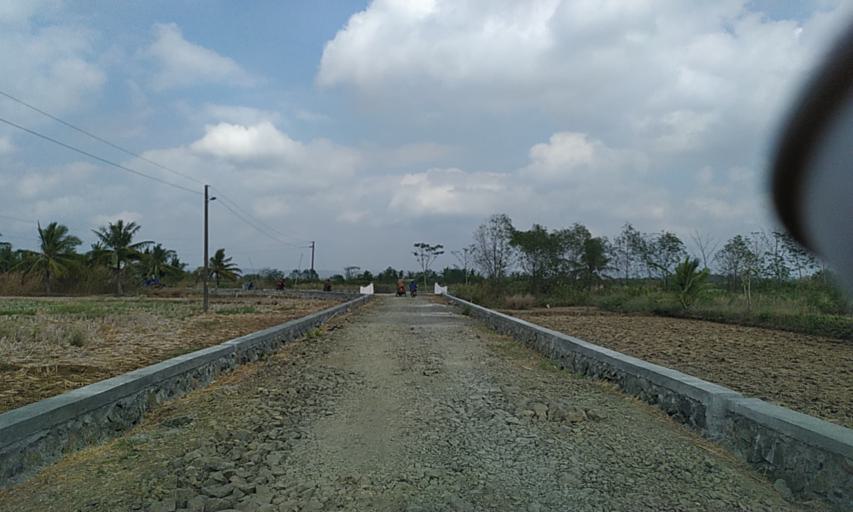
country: ID
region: Central Java
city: Karanganyar
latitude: -7.6469
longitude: 108.8350
